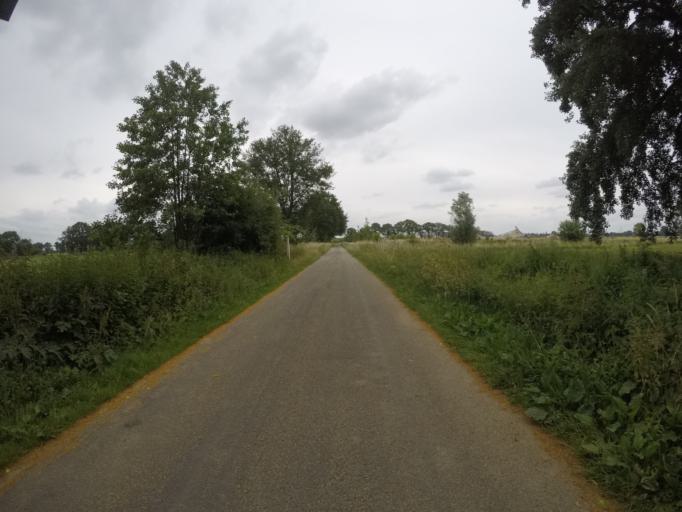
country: DE
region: North Rhine-Westphalia
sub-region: Regierungsbezirk Munster
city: Isselburg
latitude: 51.8477
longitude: 6.4491
